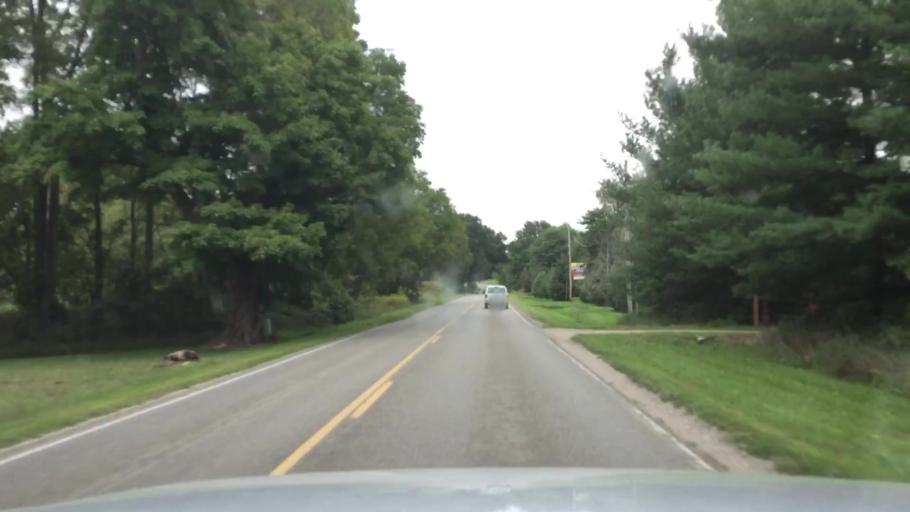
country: US
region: Michigan
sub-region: Genesee County
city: Argentine
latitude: 42.8177
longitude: -83.9389
